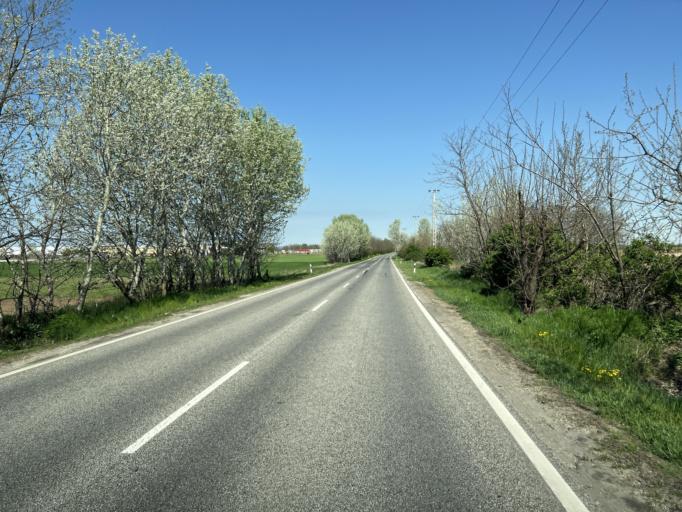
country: HU
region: Pest
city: Alsonemedi
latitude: 47.3458
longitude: 19.1688
